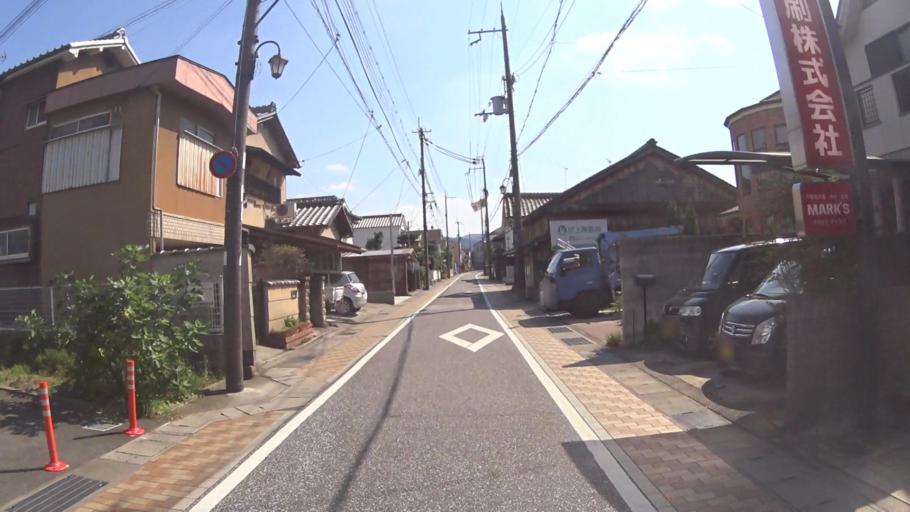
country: JP
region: Kyoto
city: Kameoka
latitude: 35.0139
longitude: 135.5769
